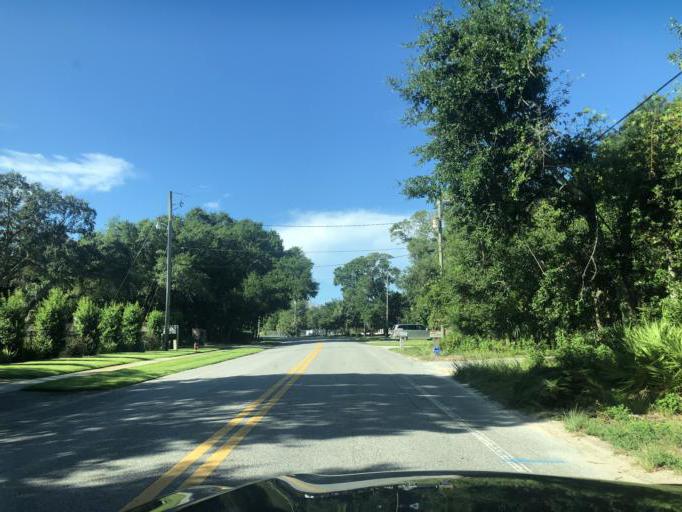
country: US
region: Florida
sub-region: Okaloosa County
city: Destin
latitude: 30.3990
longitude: -86.5118
